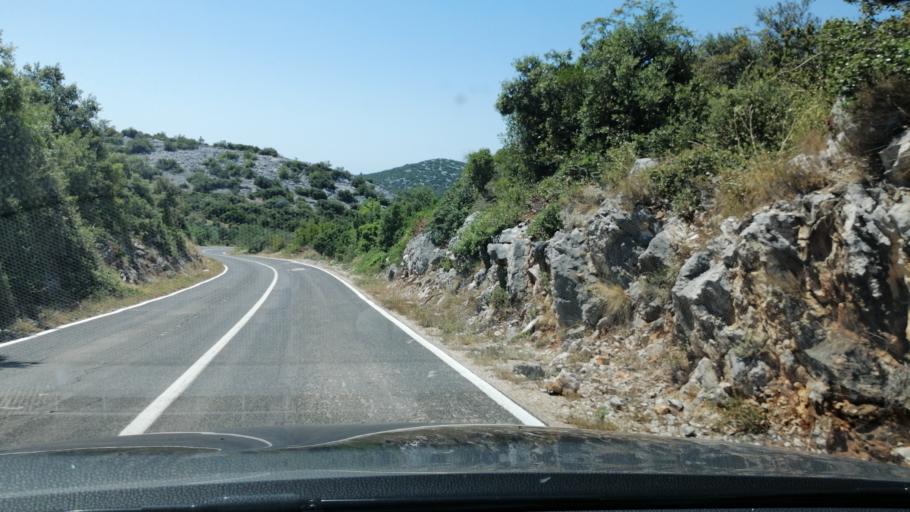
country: HR
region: Sibensko-Kniniska
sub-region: Grad Sibenik
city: Pirovac
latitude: 43.8551
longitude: 15.6908
